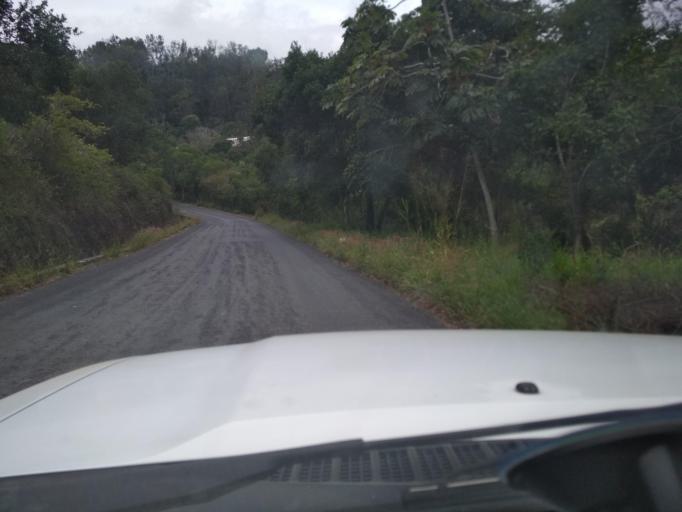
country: MX
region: Veracruz
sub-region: Emiliano Zapata
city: Dos Rios
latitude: 19.5273
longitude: -96.7977
